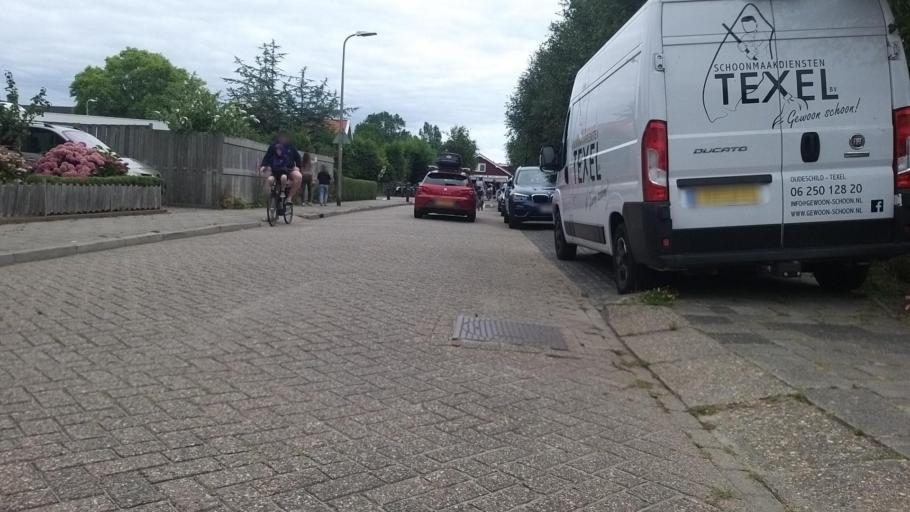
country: NL
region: North Holland
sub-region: Gemeente Texel
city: Den Burg
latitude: 53.1555
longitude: 4.8685
